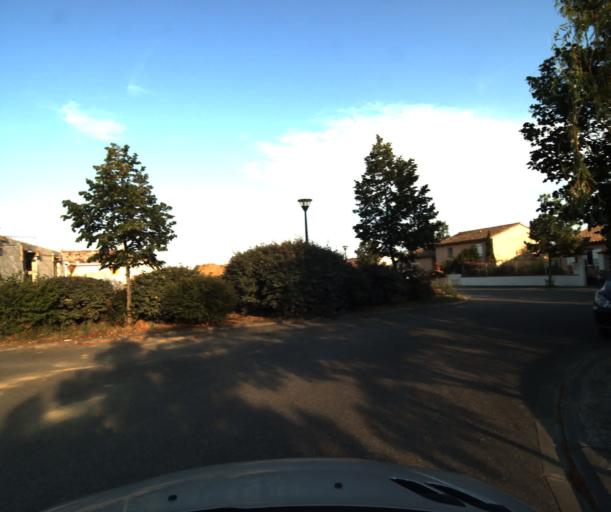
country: FR
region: Midi-Pyrenees
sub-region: Departement de la Haute-Garonne
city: Lacroix-Falgarde
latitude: 43.4841
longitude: 1.3919
